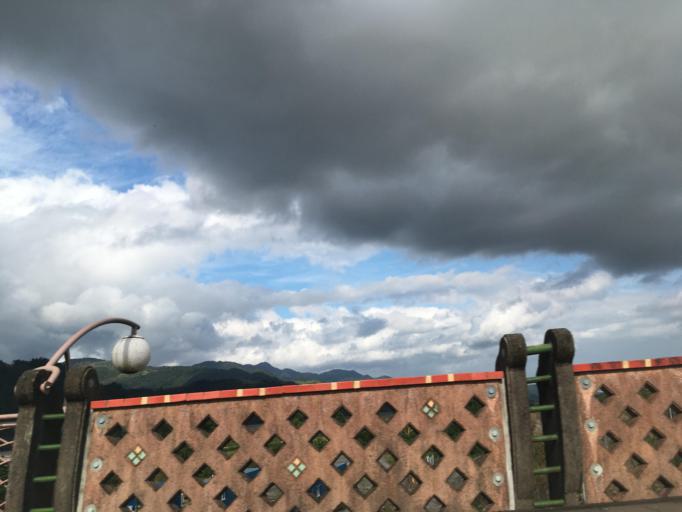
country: TW
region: Taiwan
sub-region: Yilan
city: Yilan
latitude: 24.6676
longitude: 121.6133
